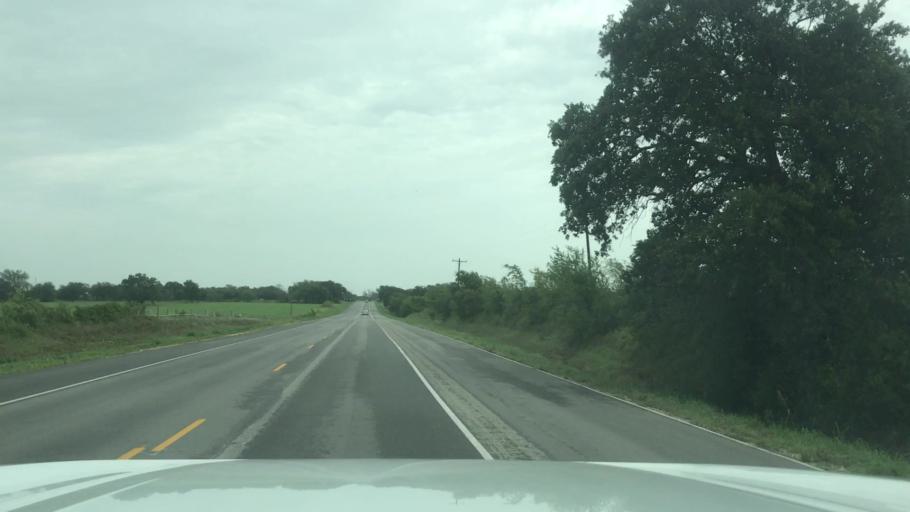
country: US
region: Texas
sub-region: Eastland County
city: Gorman
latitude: 32.2219
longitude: -98.6923
